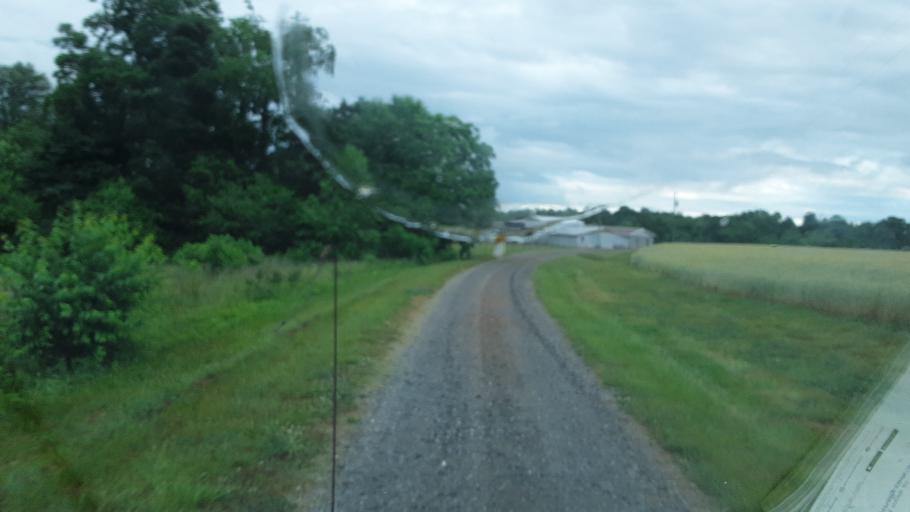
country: US
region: North Carolina
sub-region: Yadkin County
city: Jonesville
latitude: 36.0612
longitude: -80.8269
